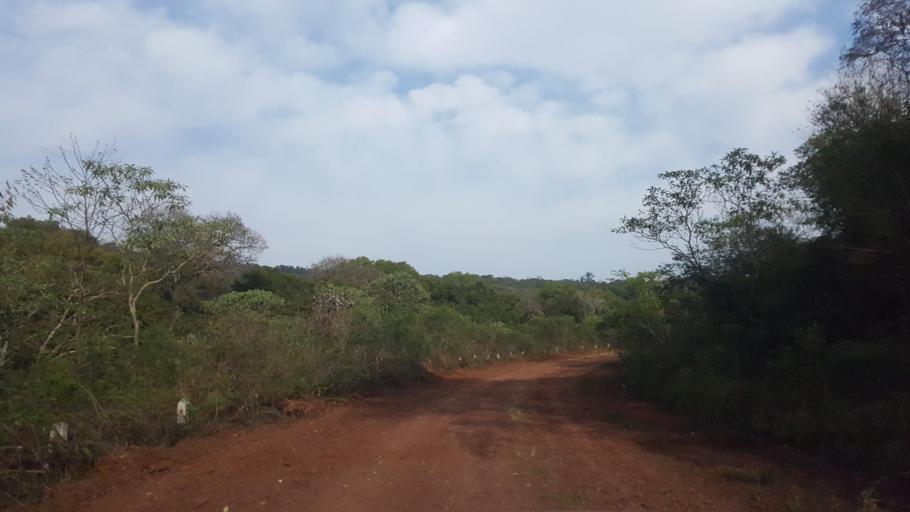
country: AR
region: Misiones
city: Capiovi
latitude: -26.9035
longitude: -55.1072
